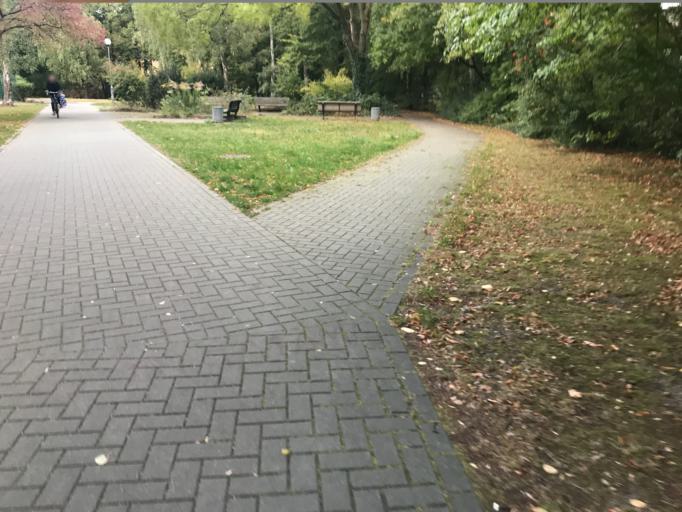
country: DE
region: Berlin
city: Buckow
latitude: 52.4348
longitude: 13.4505
